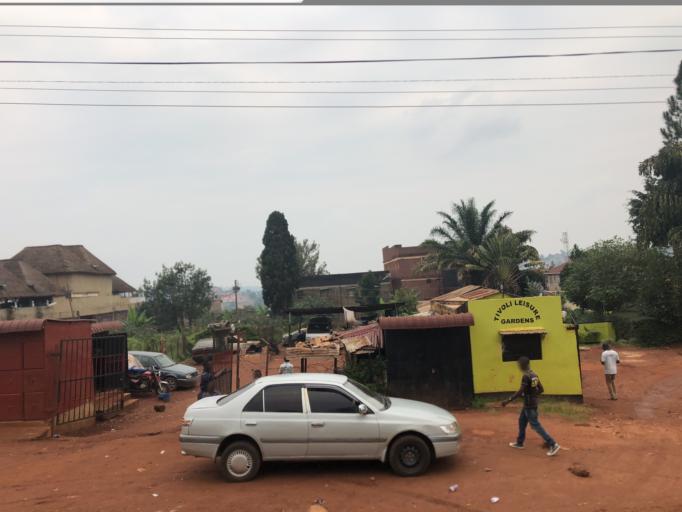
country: UG
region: Central Region
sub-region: Mukono District
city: Mukono
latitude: 0.3591
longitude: 32.7471
